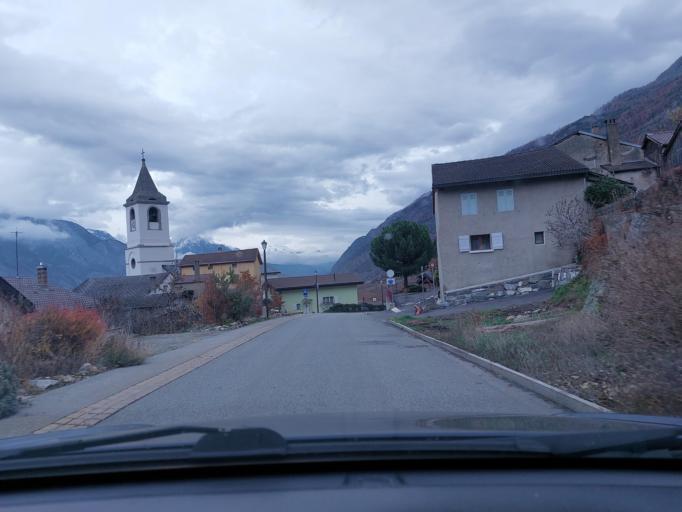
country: CH
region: Valais
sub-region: Martigny District
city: Saxon
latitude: 46.1445
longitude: 7.1799
